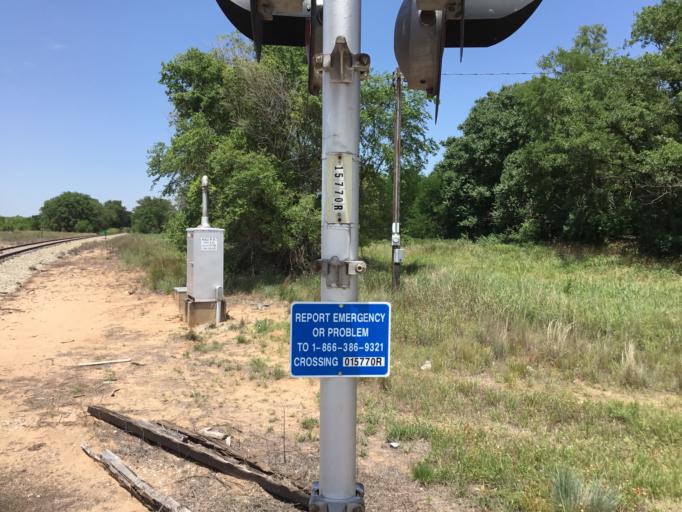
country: US
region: Kansas
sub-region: Harper County
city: Harper
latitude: 37.4574
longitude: -98.0864
